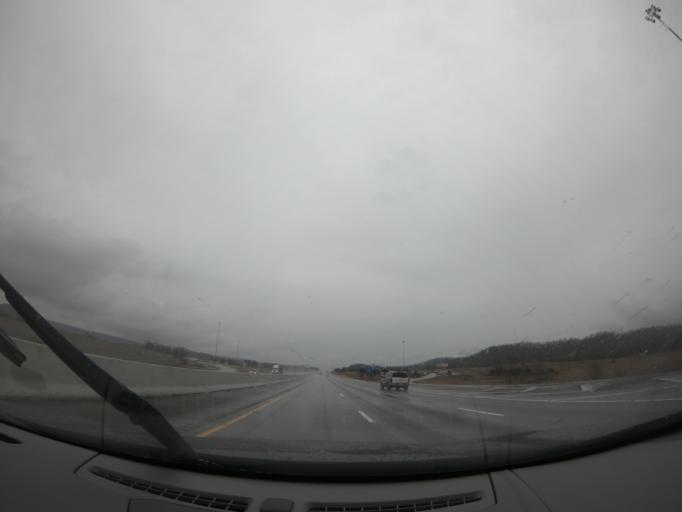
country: US
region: Kentucky
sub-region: Hart County
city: Munfordville
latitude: 37.2431
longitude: -85.9273
